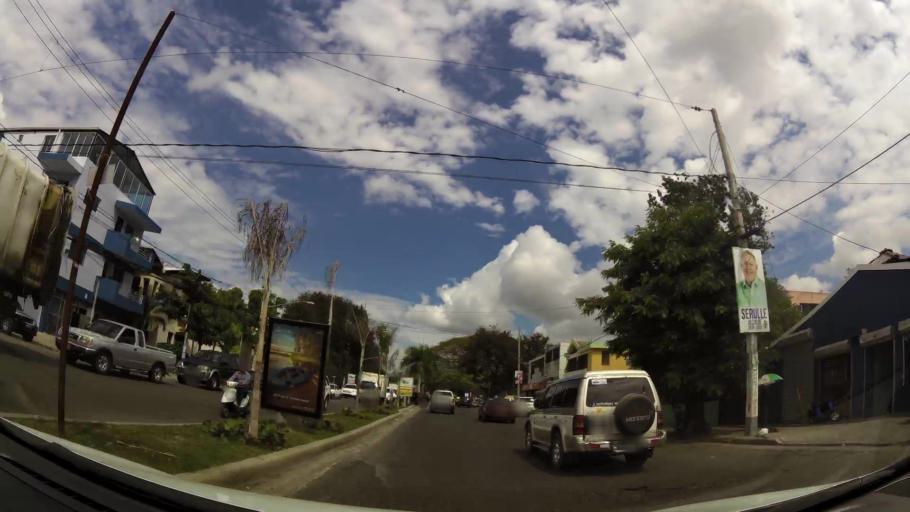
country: DO
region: Santiago
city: Santiago de los Caballeros
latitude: 19.4658
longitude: -70.7115
